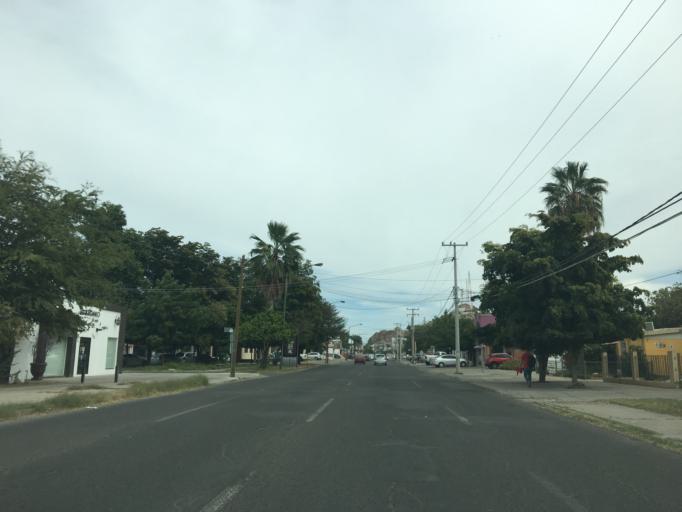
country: MX
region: Sonora
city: Hermosillo
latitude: 29.0738
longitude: -110.9678
